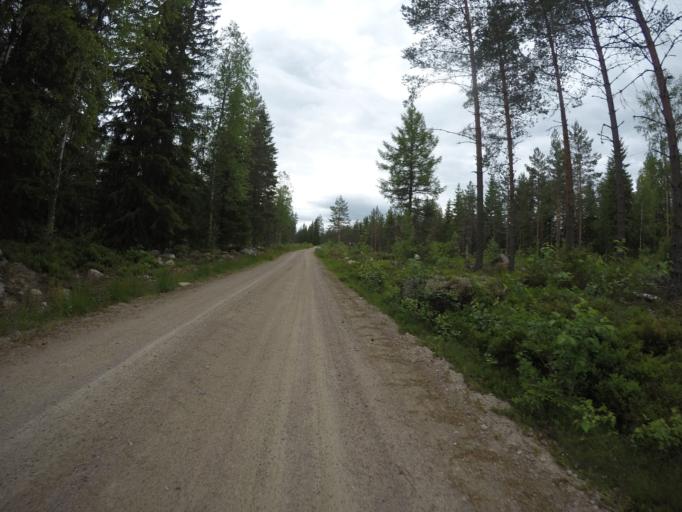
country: SE
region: Dalarna
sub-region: Ludvika Kommun
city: Abborrberget
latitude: 60.0952
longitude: 14.5466
